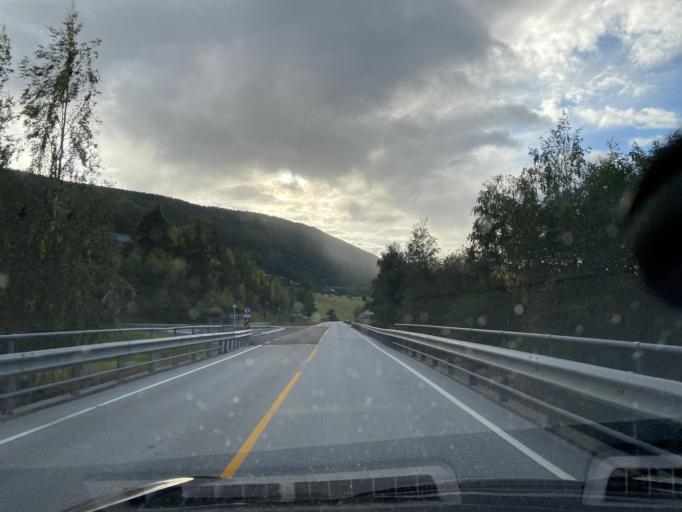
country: NO
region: Oppland
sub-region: Vaga
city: Vagamo
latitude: 61.8490
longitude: 8.9610
